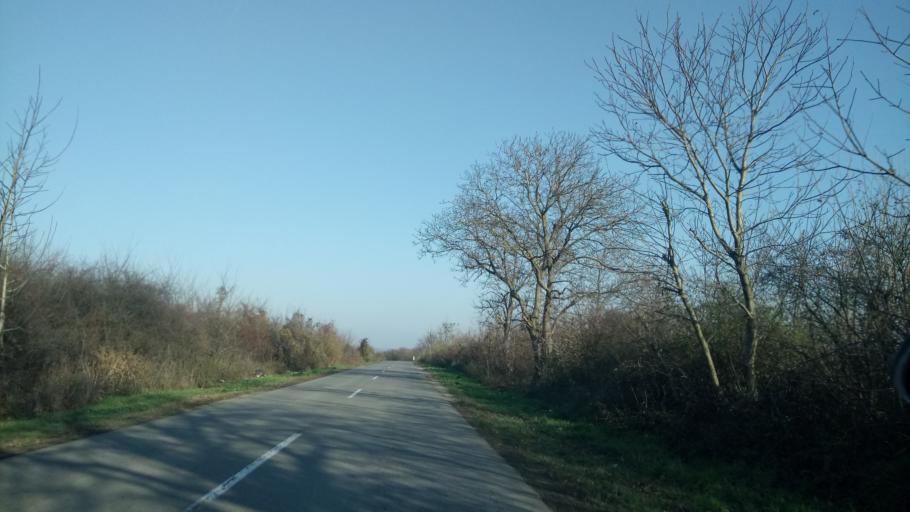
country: RS
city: Beska
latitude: 45.1150
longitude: 20.0471
